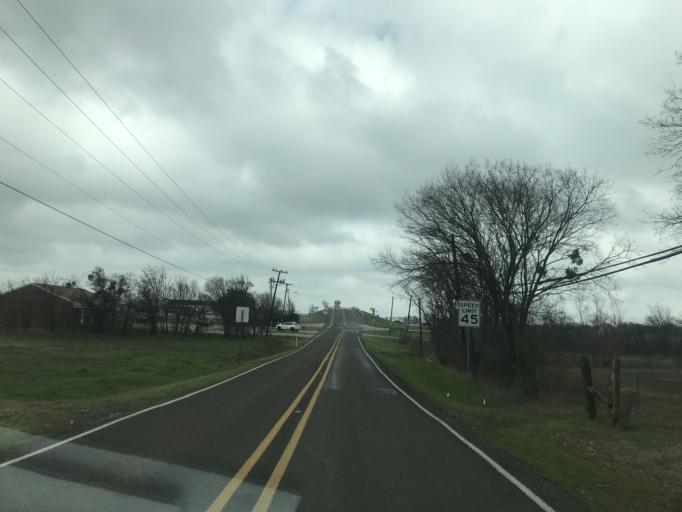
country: US
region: Texas
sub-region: Ellis County
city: Palmer
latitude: 32.4325
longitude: -96.6633
